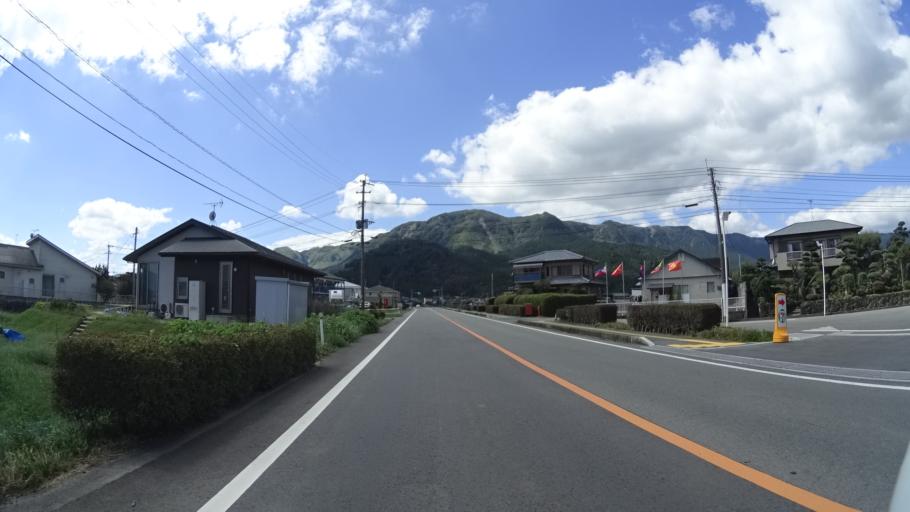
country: JP
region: Kumamoto
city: Aso
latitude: 32.9687
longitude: 131.0399
